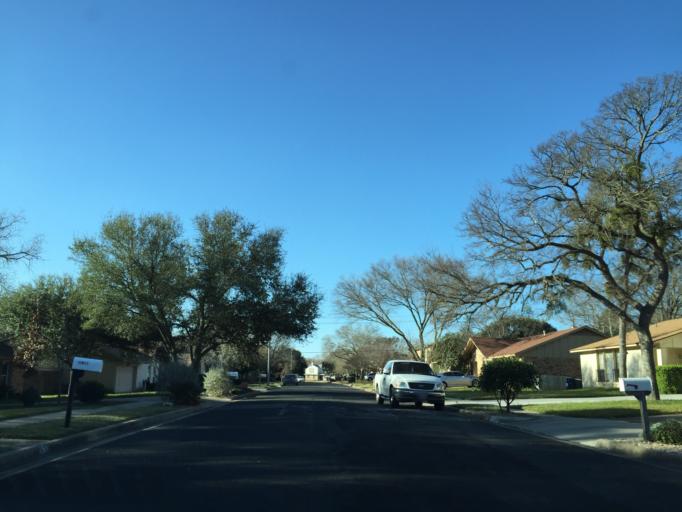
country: US
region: Texas
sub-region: Williamson County
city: Jollyville
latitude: 30.4113
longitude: -97.7400
